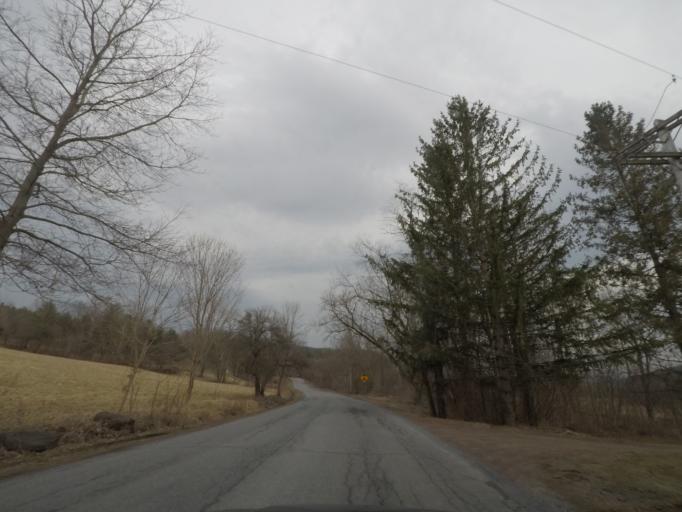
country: US
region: New York
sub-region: Rensselaer County
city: Hoosick Falls
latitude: 42.9470
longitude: -73.3732
